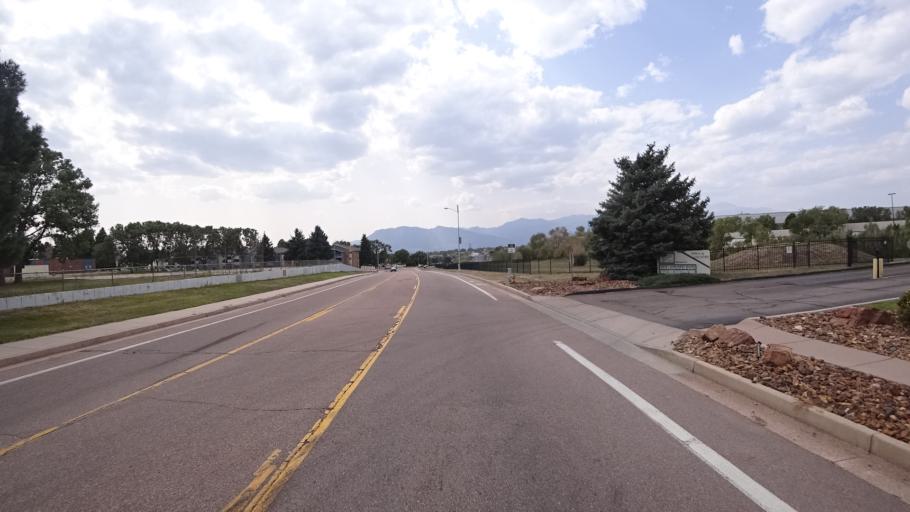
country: US
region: Colorado
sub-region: El Paso County
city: Cimarron Hills
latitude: 38.8369
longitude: -104.7519
